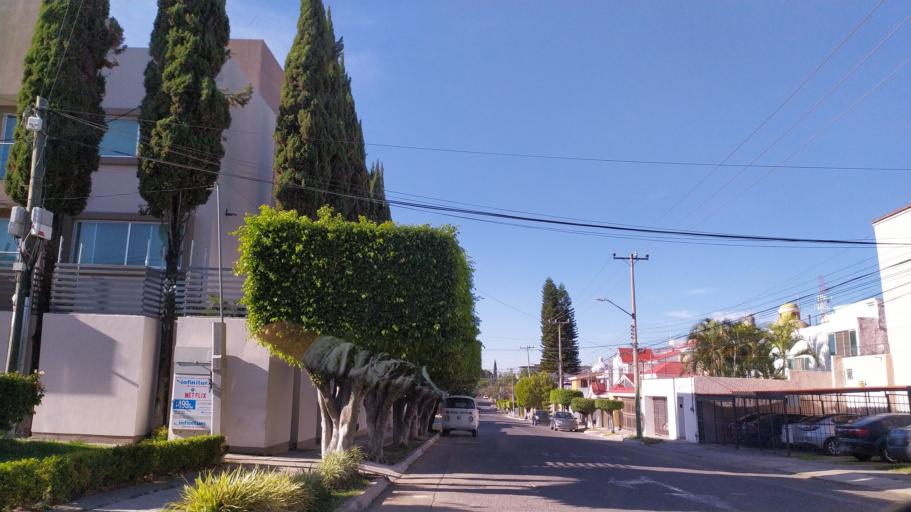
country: MX
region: Jalisco
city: Guadalajara
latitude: 20.6639
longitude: -103.4287
